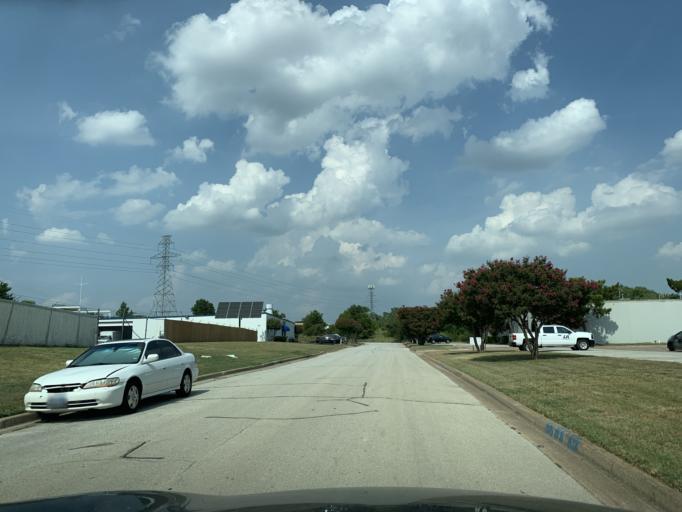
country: US
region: Texas
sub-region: Tarrant County
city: Richland Hills
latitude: 32.8067
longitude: -97.2089
